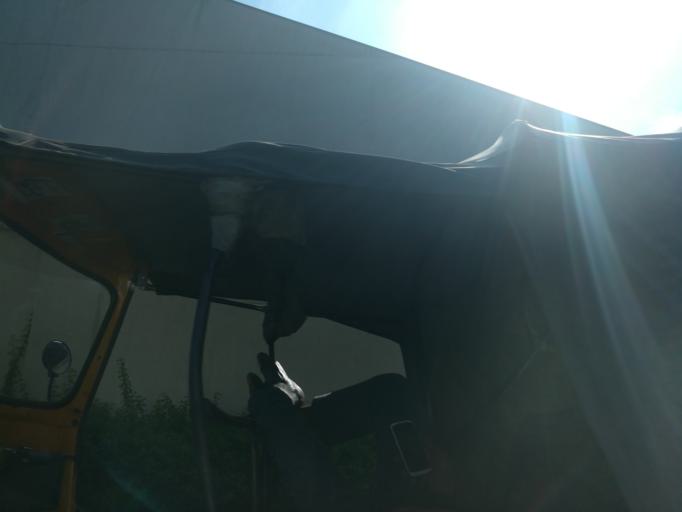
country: NG
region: Lagos
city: Ikeja
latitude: 6.6018
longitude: 3.3407
